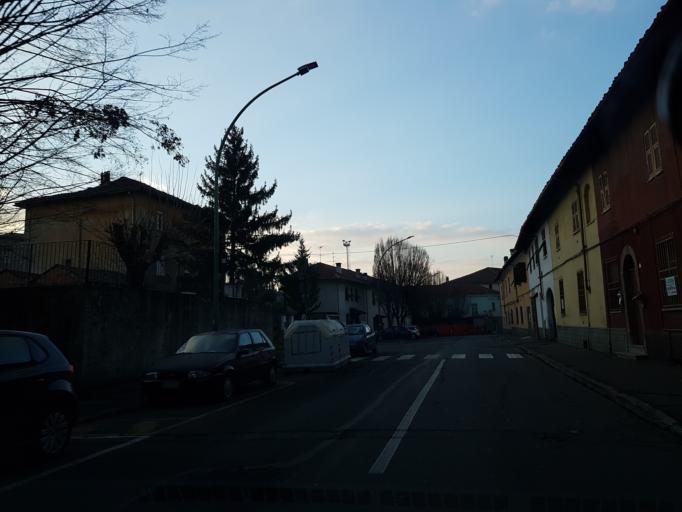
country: IT
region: Piedmont
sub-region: Provincia di Alessandria
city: Novi Ligure
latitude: 44.7599
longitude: 8.7941
